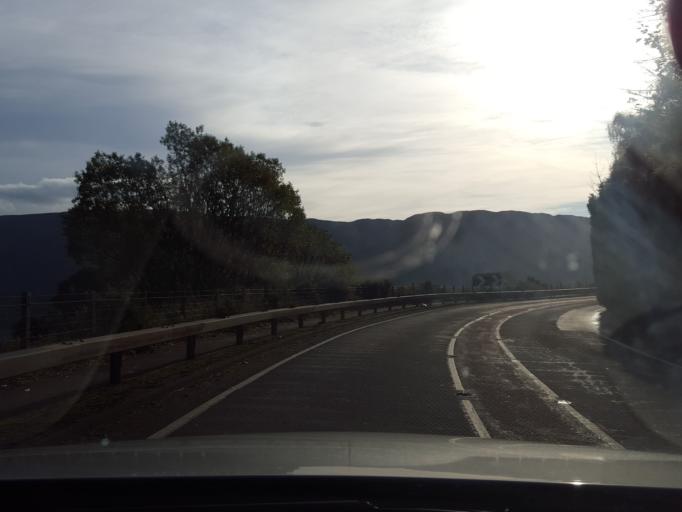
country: GB
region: Scotland
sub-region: Highland
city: Beauly
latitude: 57.3271
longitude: -4.4457
